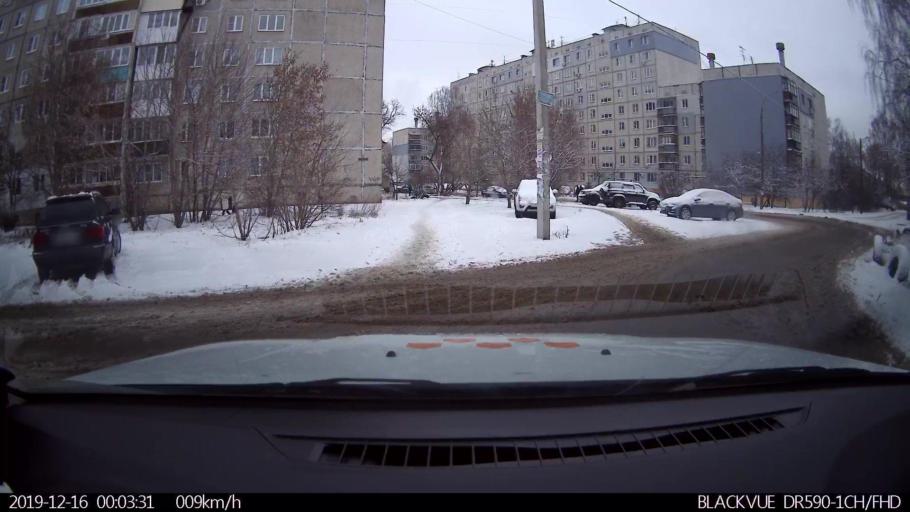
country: RU
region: Nizjnij Novgorod
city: Gorbatovka
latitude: 56.3582
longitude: 43.8442
